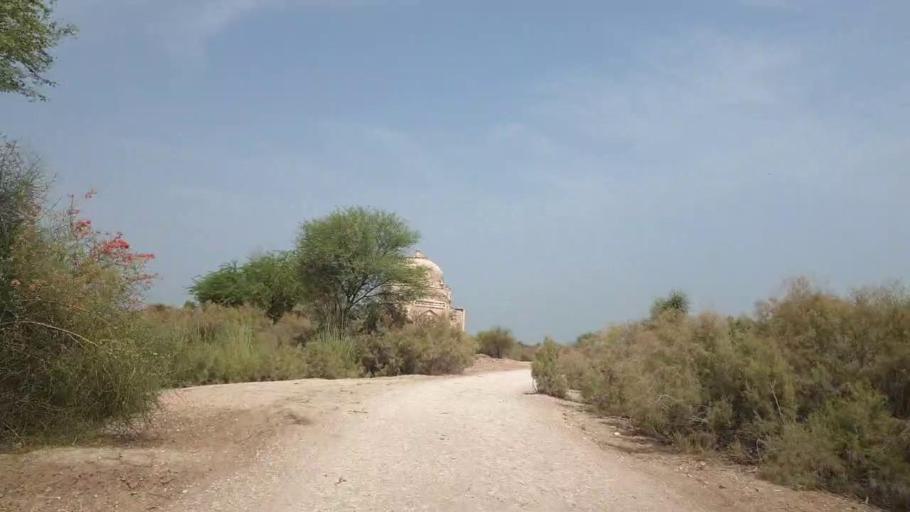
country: PK
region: Sindh
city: Dokri
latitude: 27.3962
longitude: 68.2595
